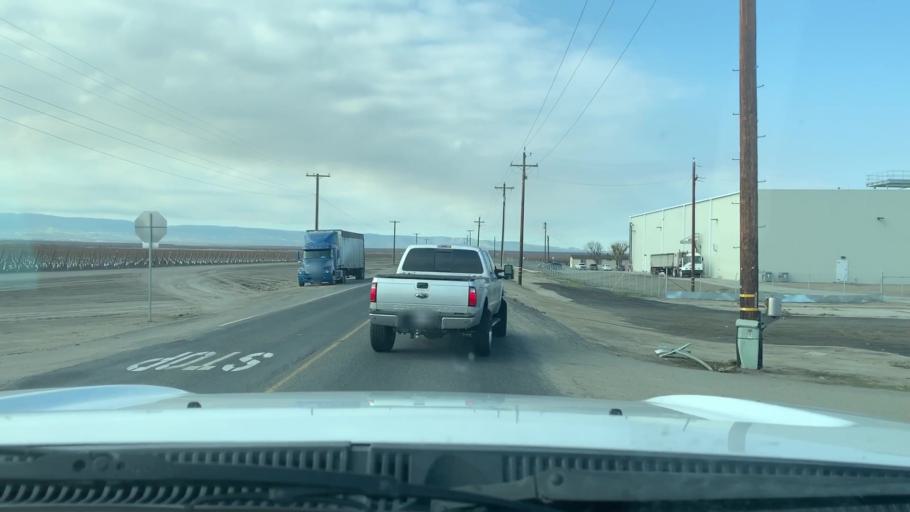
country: US
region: California
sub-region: Kern County
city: Lost Hills
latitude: 35.4995
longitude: -119.6028
